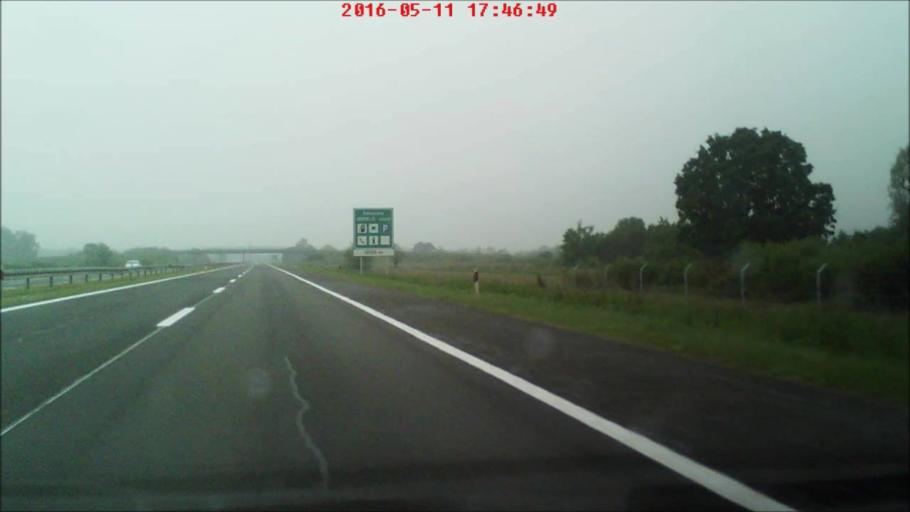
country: HR
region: Zagrebacka
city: Jakovlje
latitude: 45.9406
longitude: 15.8302
